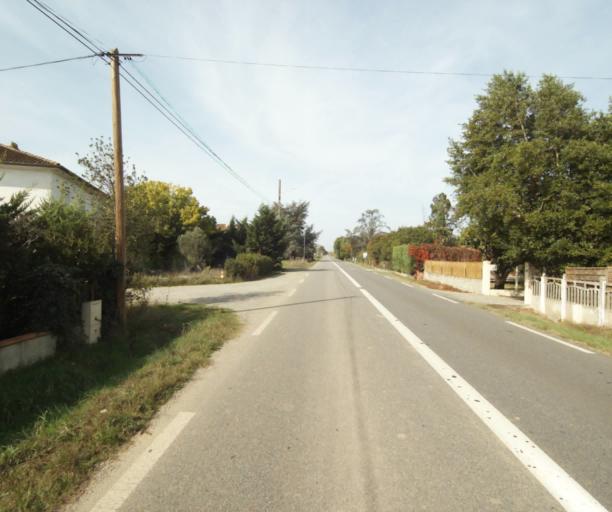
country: FR
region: Midi-Pyrenees
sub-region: Departement du Tarn-et-Garonne
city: Orgueil
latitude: 43.9232
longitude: 1.3920
